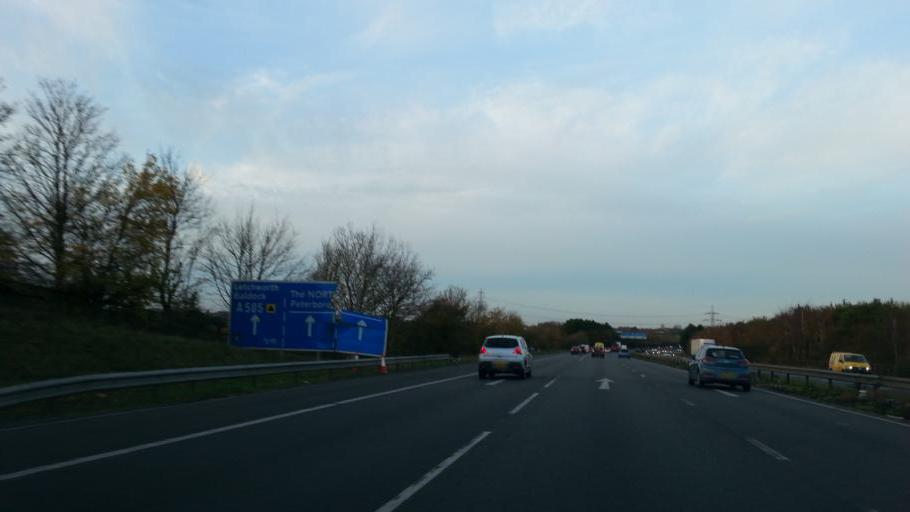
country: GB
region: England
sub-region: Hertfordshire
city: Letchworth Garden City
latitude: 51.9508
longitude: -0.2115
